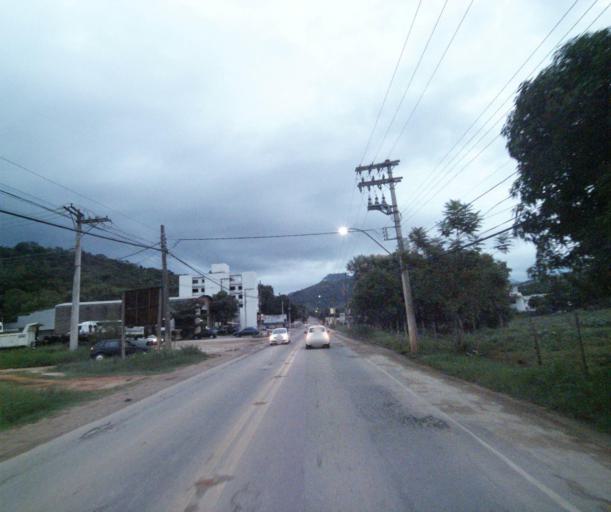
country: BR
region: Espirito Santo
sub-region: Castelo
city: Castelo
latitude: -20.6303
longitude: -41.2040
